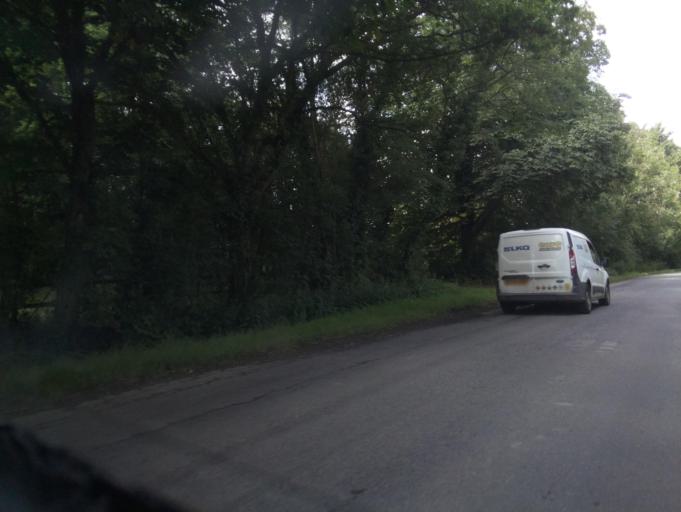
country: GB
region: England
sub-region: Wiltshire
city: Minety
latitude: 51.6149
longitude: -1.9872
